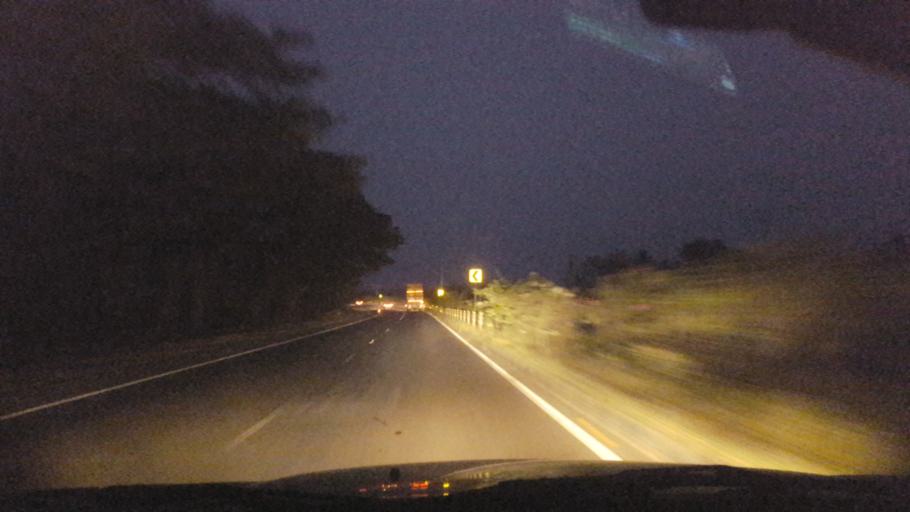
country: IN
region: Andhra Pradesh
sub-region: East Godavari
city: Peddapuram
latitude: 17.1372
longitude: 81.9651
